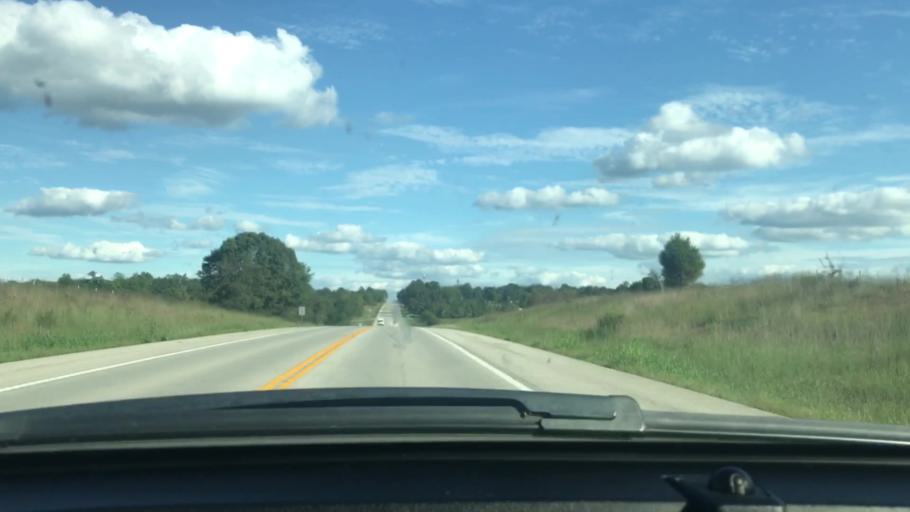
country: US
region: Missouri
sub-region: Howell County
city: West Plains
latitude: 36.6565
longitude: -91.7002
